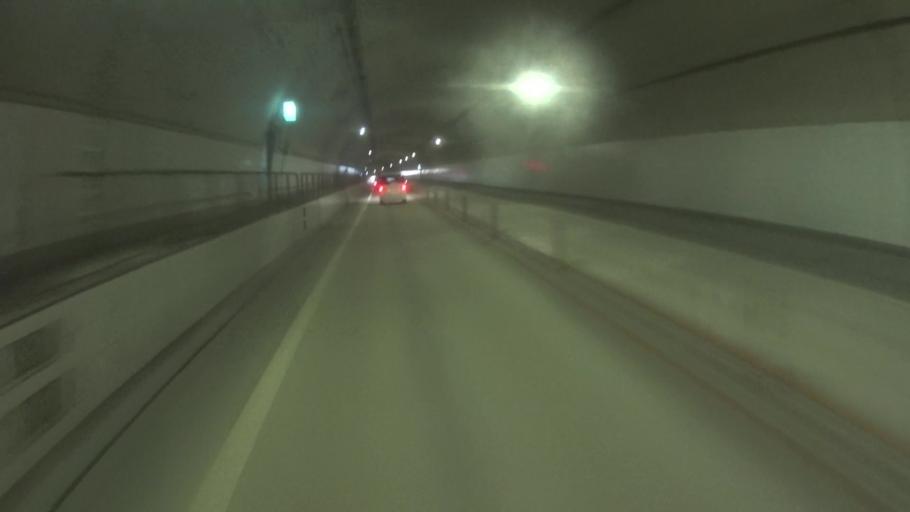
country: JP
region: Kyoto
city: Miyazu
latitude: 35.5355
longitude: 135.1636
